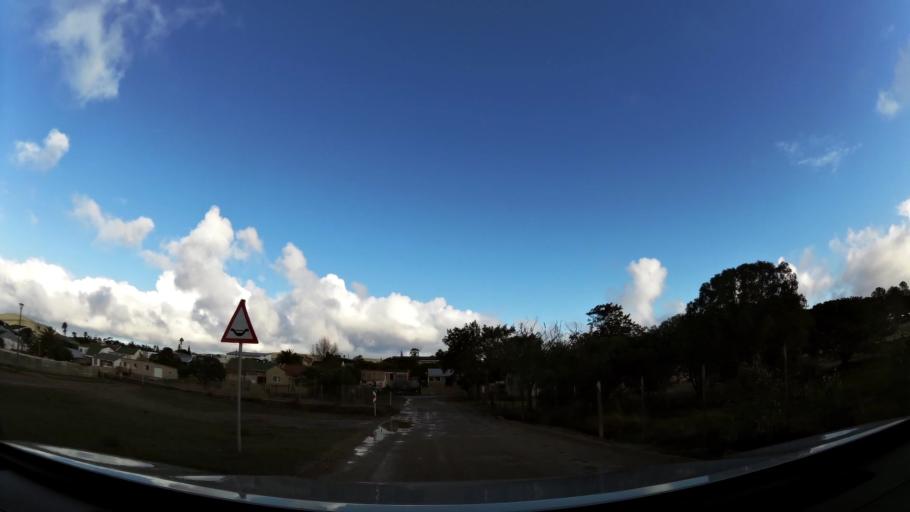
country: ZA
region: Western Cape
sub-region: Eden District Municipality
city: Riversdale
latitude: -34.2016
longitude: 21.5819
